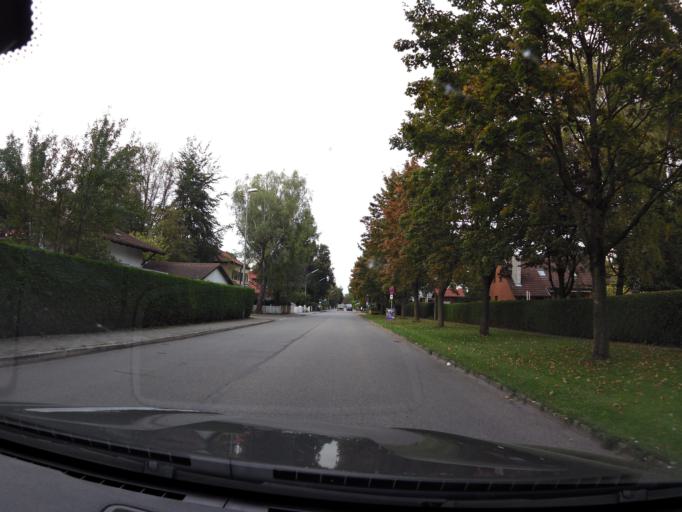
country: DE
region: Bavaria
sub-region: Upper Bavaria
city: Grobenzell
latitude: 48.1867
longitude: 11.3714
